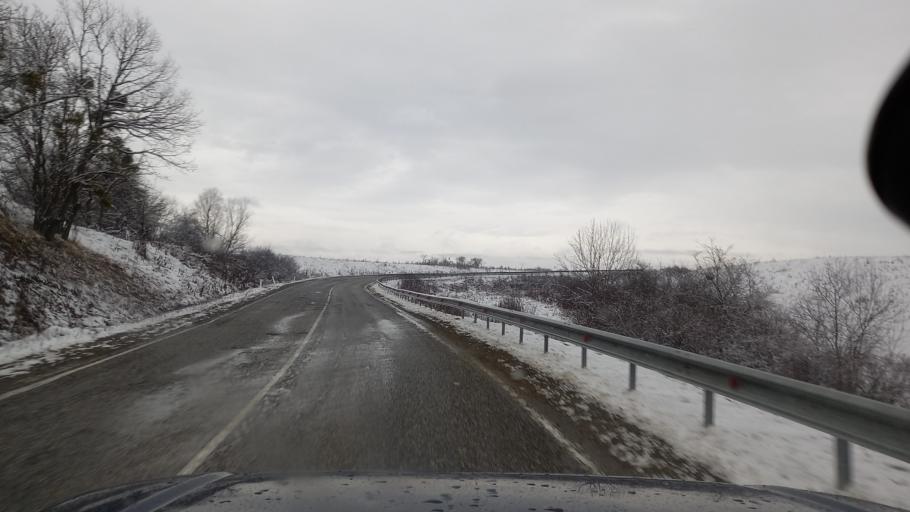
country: RU
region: Adygeya
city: Abadzekhskaya
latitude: 44.3483
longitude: 40.3355
